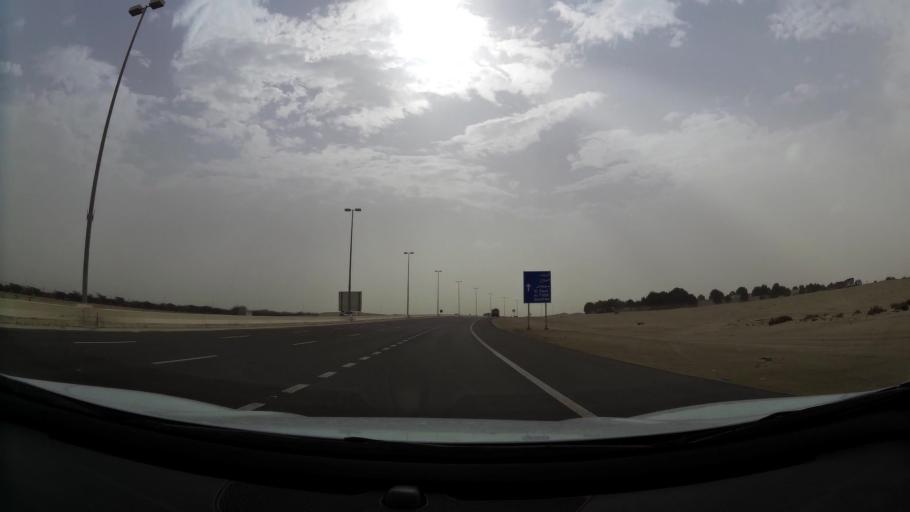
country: AE
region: Abu Dhabi
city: Abu Dhabi
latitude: 24.4755
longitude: 54.6678
